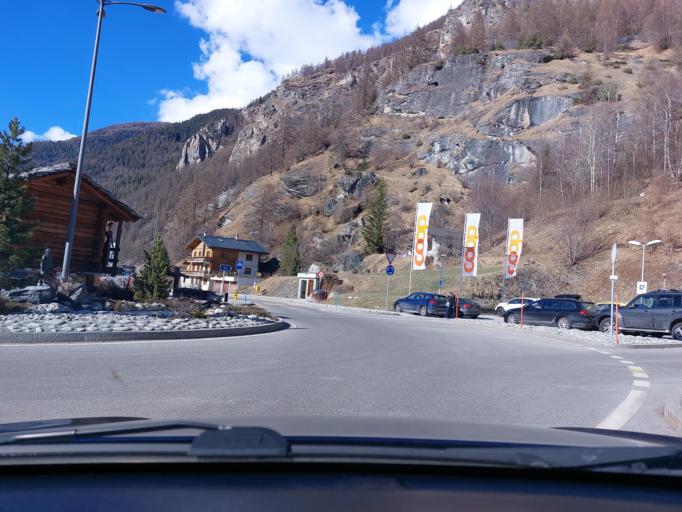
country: CH
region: Valais
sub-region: Herens District
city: Evolene
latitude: 46.1084
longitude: 7.5006
